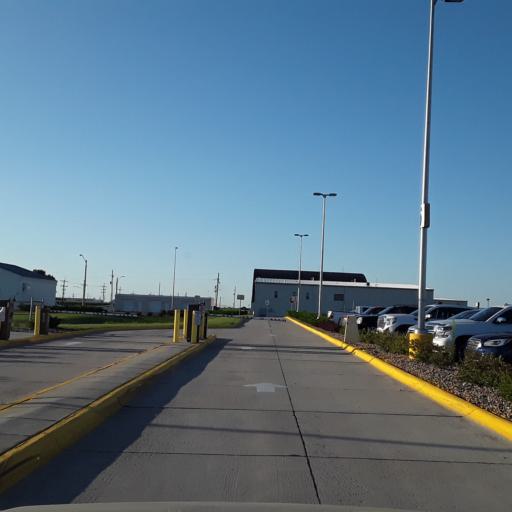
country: US
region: Nebraska
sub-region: Hall County
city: Grand Island
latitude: 40.9697
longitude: -98.3196
